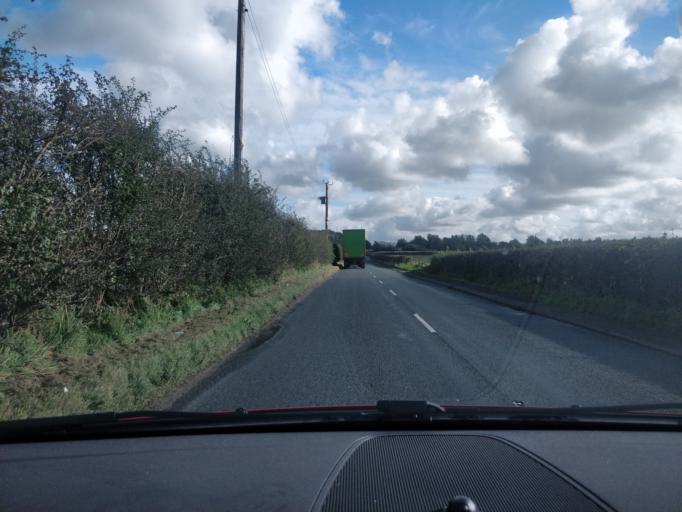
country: GB
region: England
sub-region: Lancashire
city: Ormskirk
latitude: 53.5889
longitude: -2.8723
